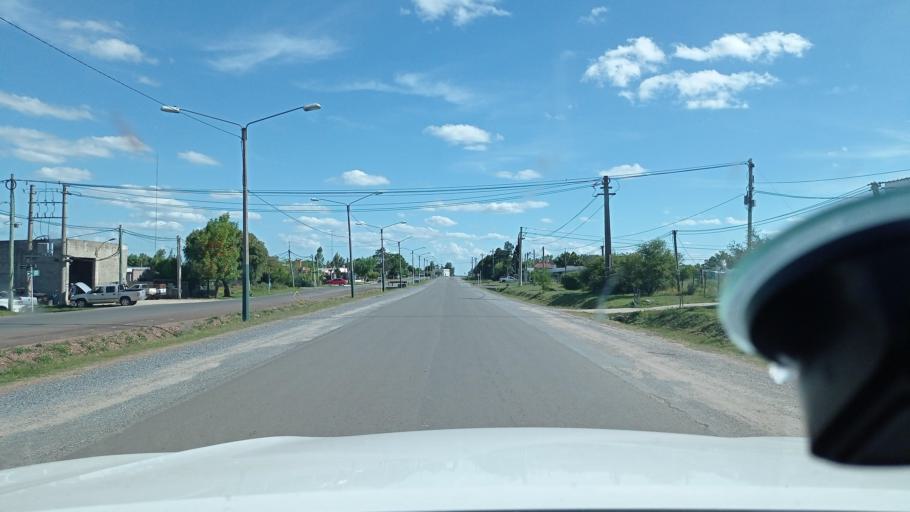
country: UY
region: Florida
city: Florida
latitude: -34.0872
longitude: -56.2377
